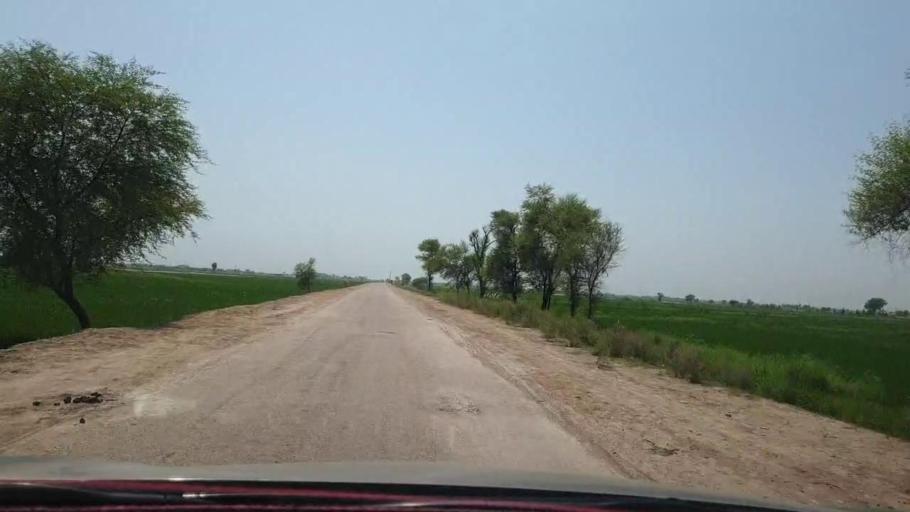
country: PK
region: Sindh
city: Warah
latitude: 27.5585
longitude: 67.7992
